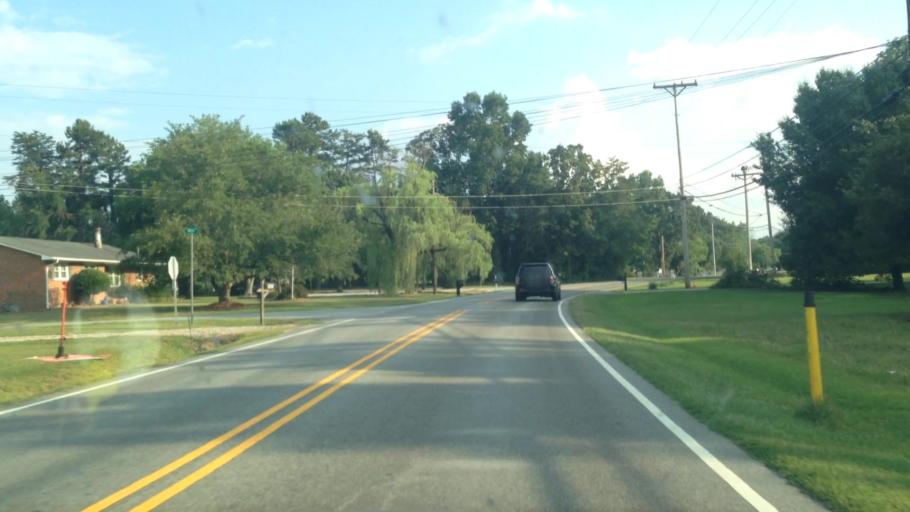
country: US
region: North Carolina
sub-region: Guilford County
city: High Point
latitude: 36.0060
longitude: -80.0608
